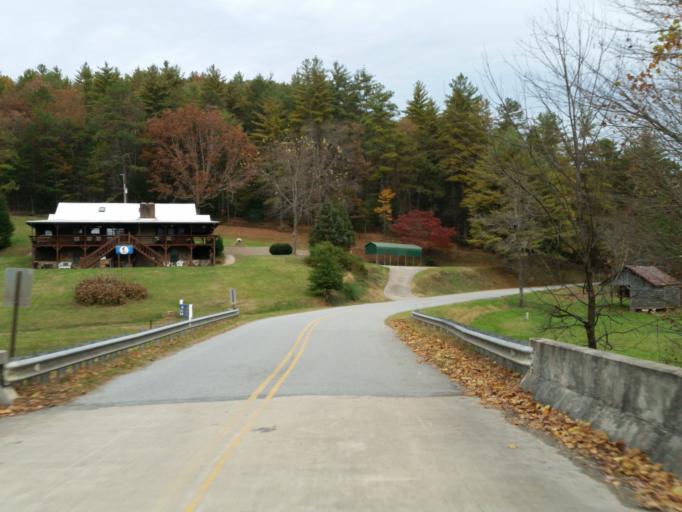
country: US
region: Georgia
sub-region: Fannin County
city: Blue Ridge
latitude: 34.7544
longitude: -84.1905
